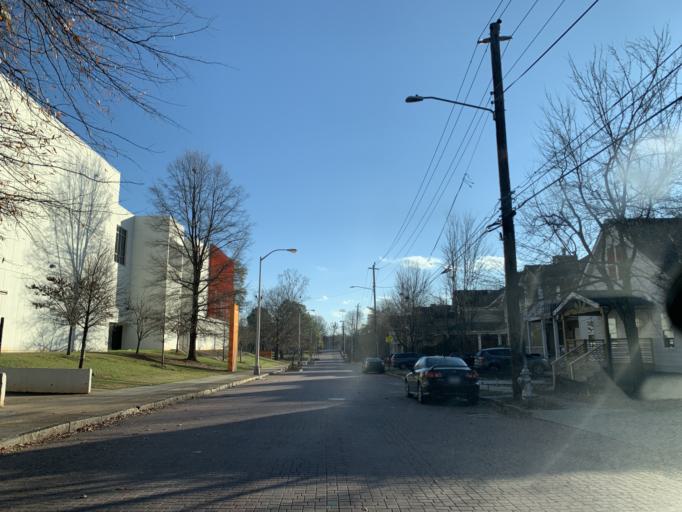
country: US
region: Georgia
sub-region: Fulton County
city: Atlanta
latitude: 33.7392
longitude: -84.3815
